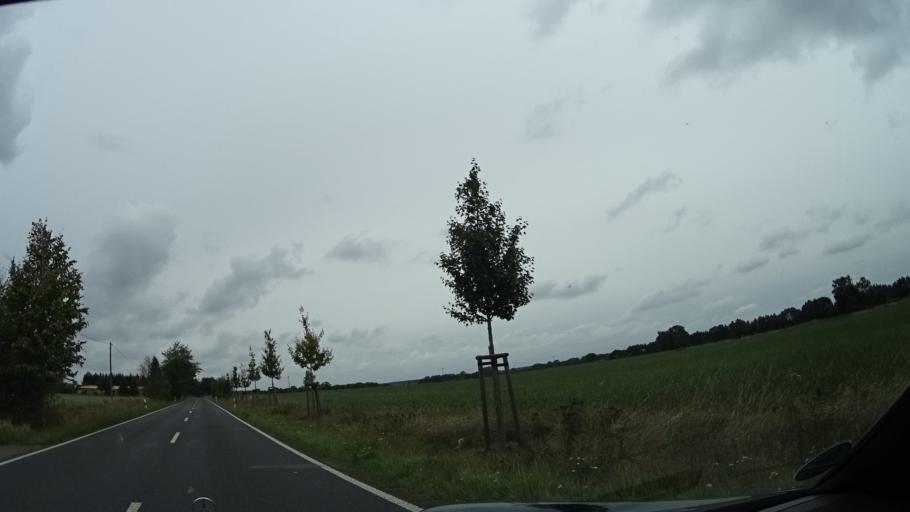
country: DE
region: Brandenburg
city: Dabergotz
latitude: 52.9359
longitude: 12.7305
